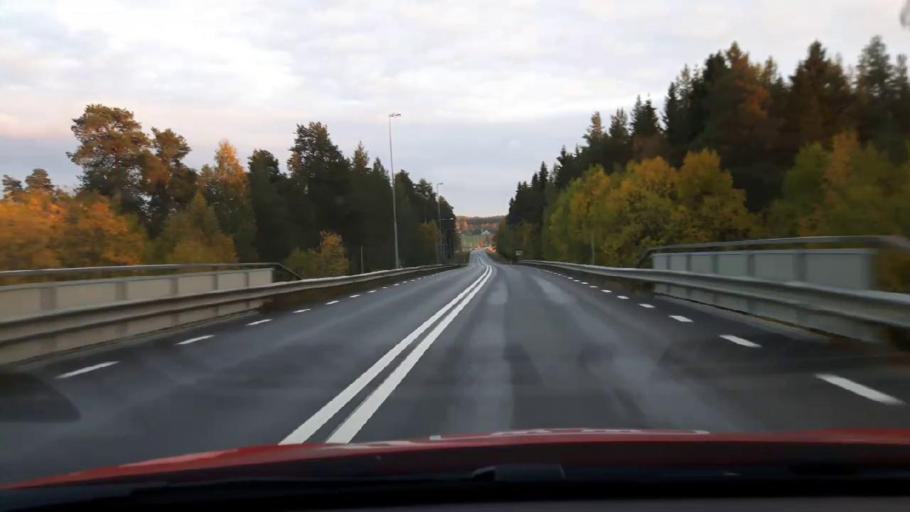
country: SE
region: Jaemtland
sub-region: OEstersunds Kommun
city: Lit
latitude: 63.3200
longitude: 14.8625
